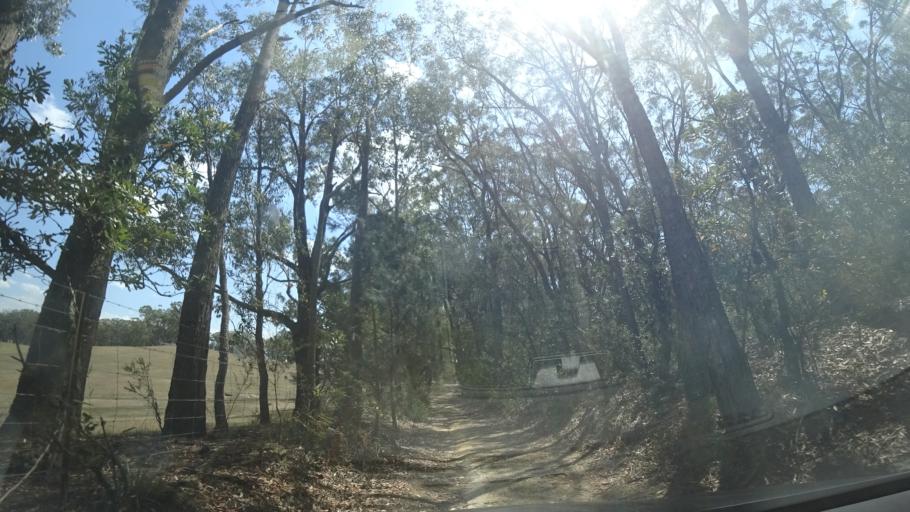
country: AU
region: New South Wales
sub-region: Wingecarribee
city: Bundanoon
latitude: -34.6390
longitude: 150.2525
